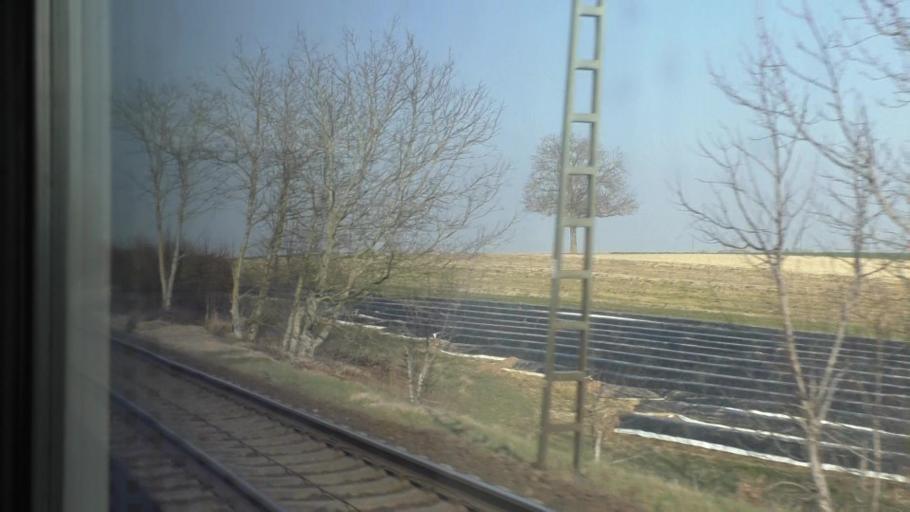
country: DE
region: Baden-Wuerttemberg
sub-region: Freiburg Region
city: Eschbach
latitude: 47.8947
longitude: 7.6618
